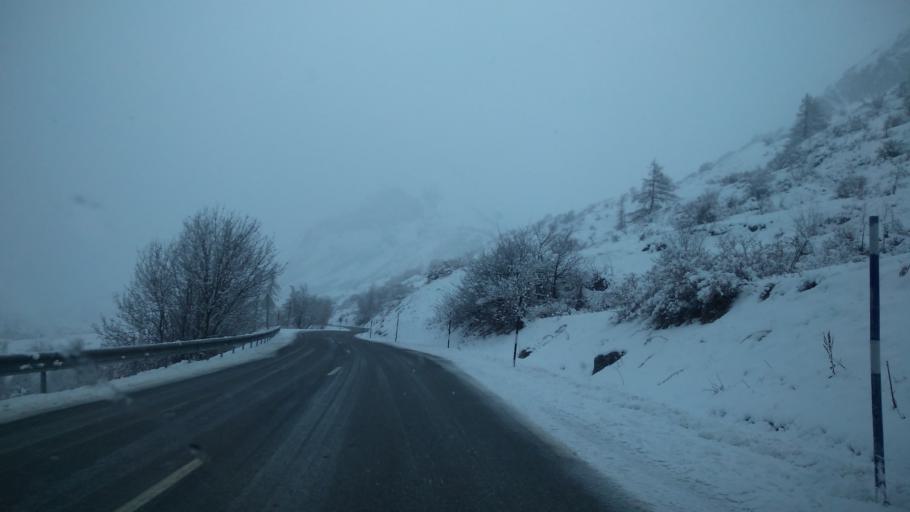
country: FR
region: Provence-Alpes-Cote d'Azur
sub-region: Departement des Hautes-Alpes
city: Le Monetier-les-Bains
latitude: 45.0091
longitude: 6.4711
